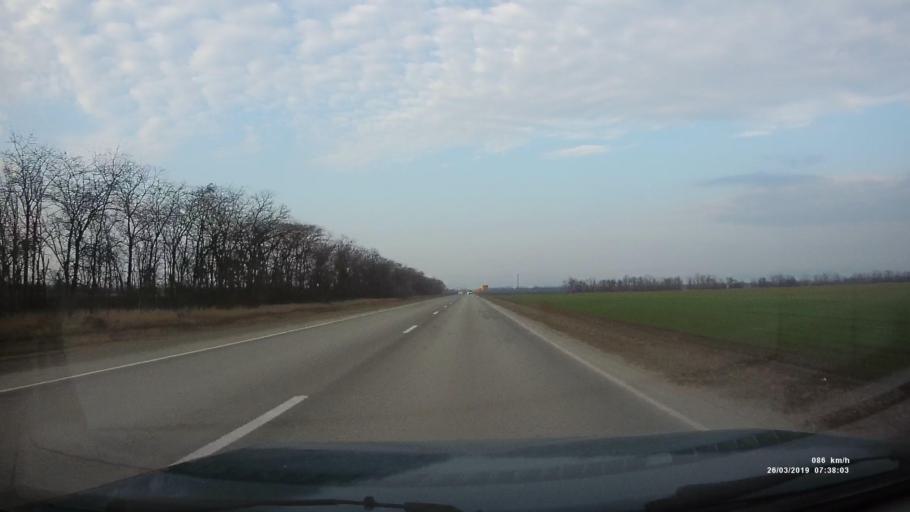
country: RU
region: Rostov
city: Novobessergenovka
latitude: 47.2010
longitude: 38.6896
